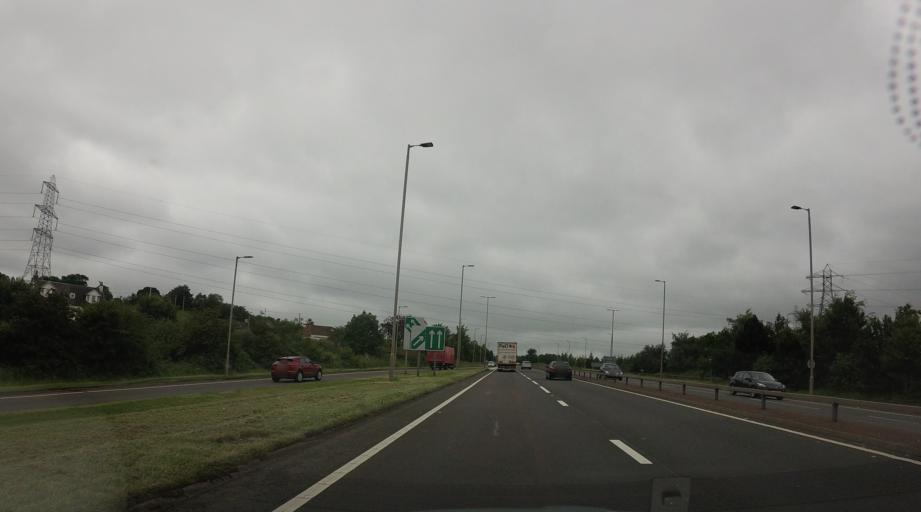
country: GB
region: Scotland
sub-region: South Lanarkshire
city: High Blantyre
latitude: 55.7827
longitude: -4.1080
